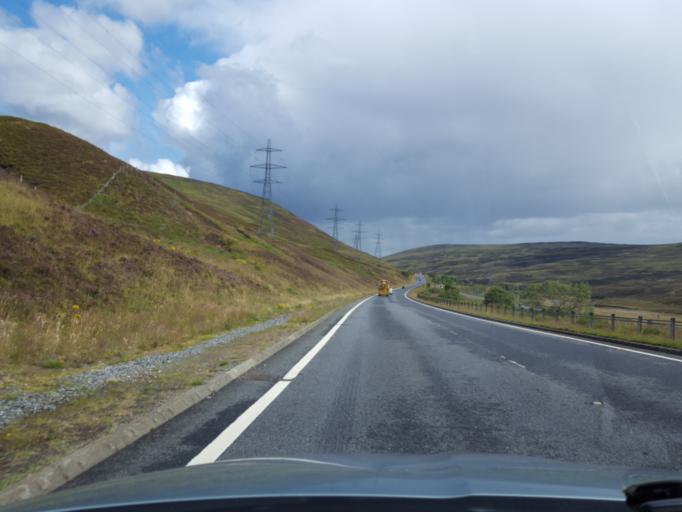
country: GB
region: Scotland
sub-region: Highland
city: Kingussie
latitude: 56.8242
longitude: -4.1990
